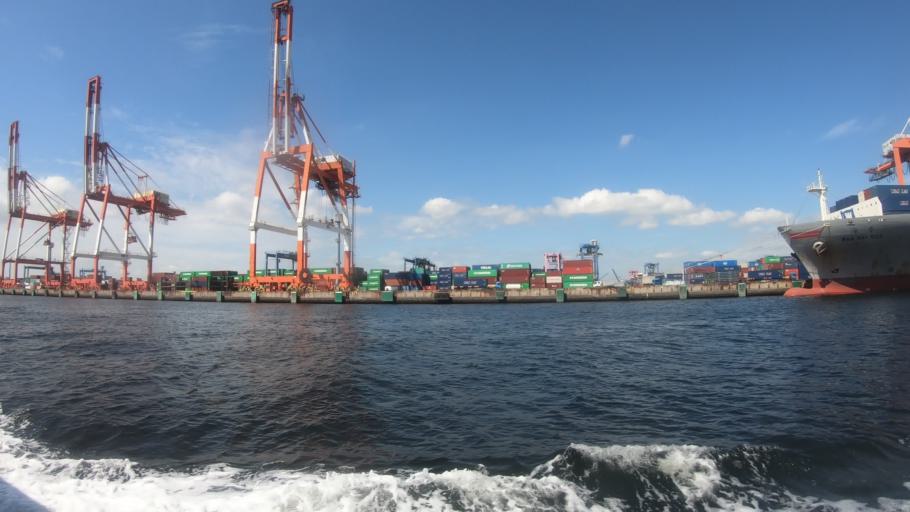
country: JP
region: Kanagawa
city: Yokohama
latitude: 35.4380
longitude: 139.6808
